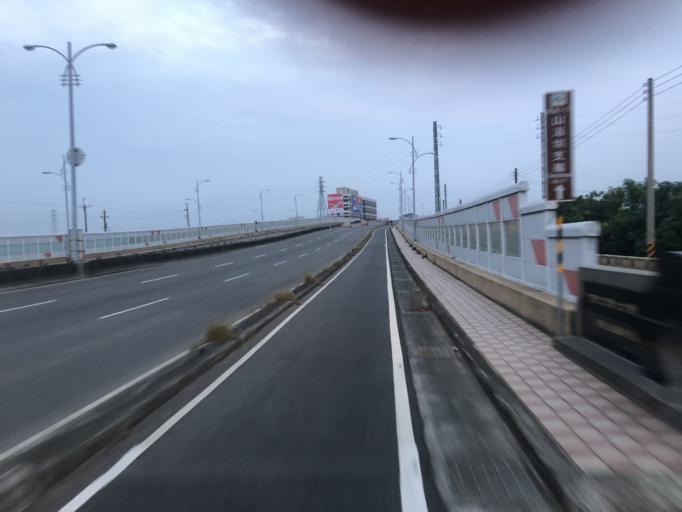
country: TW
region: Taiwan
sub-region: Tainan
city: Tainan
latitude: 23.1073
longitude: 120.2987
